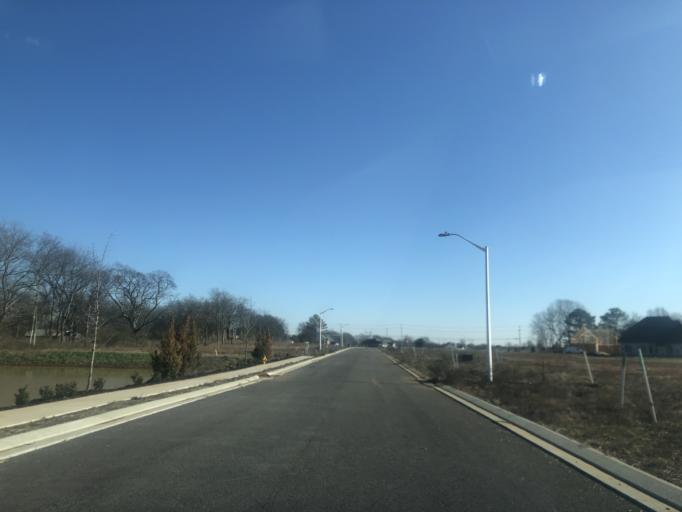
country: US
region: Tennessee
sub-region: Rutherford County
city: Smyrna
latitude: 35.8979
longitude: -86.4814
